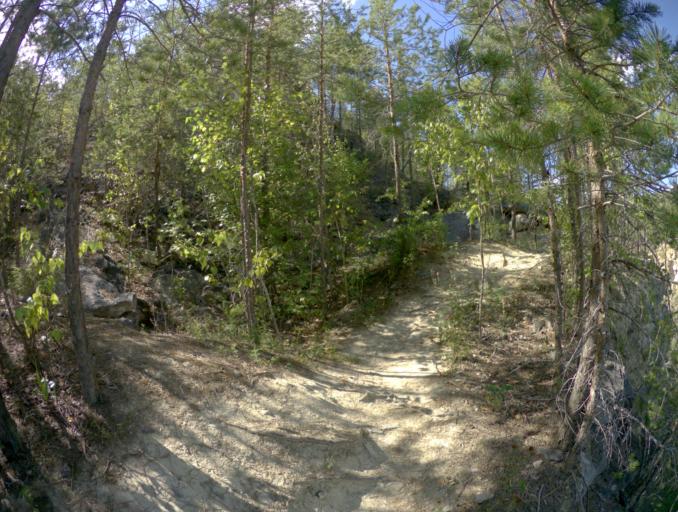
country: RU
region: Vladimir
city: Krasnyy Bogatyr'
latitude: 56.0101
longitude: 41.0626
